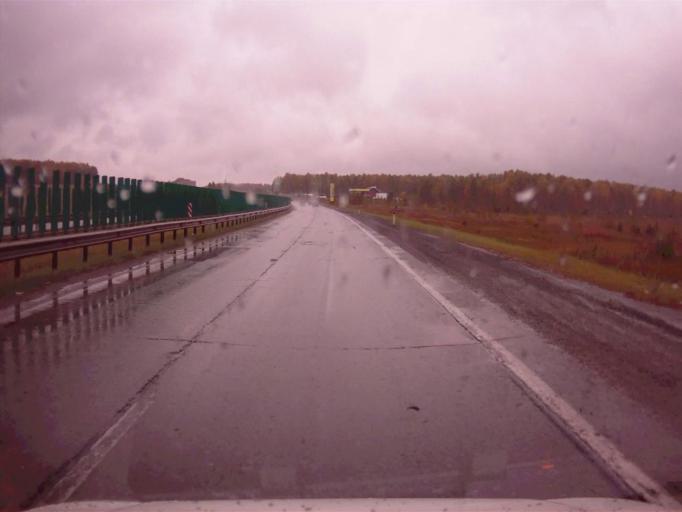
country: RU
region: Chelyabinsk
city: Dolgoderevenskoye
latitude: 55.3229
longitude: 61.3324
